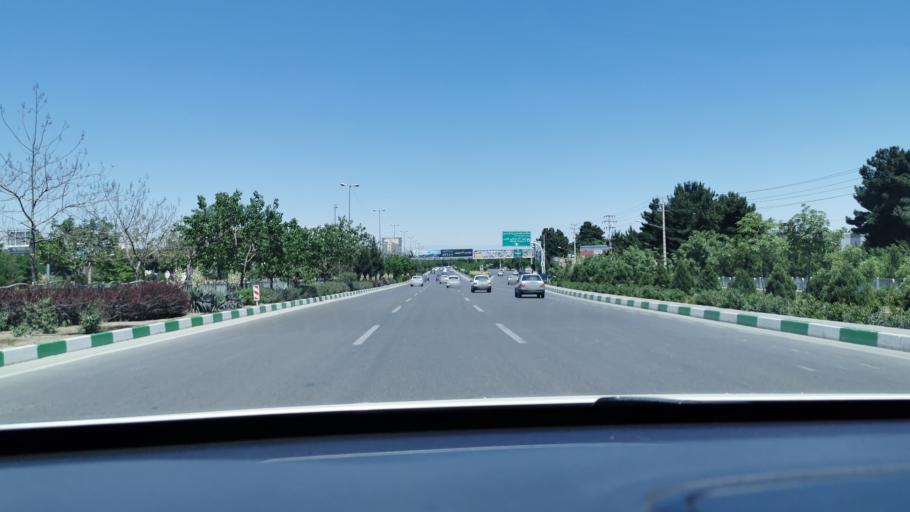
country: IR
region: Razavi Khorasan
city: Mashhad
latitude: 36.2544
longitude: 59.6175
